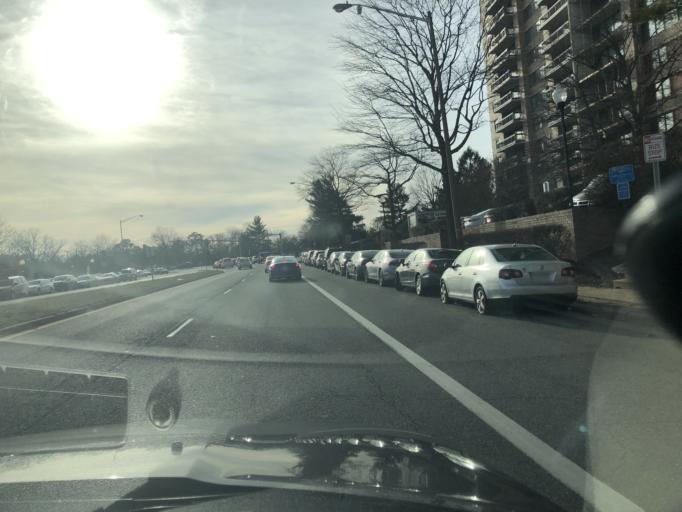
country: US
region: Virginia
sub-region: Fairfax County
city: Baileys Crossroads
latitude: 38.8417
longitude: -77.1197
